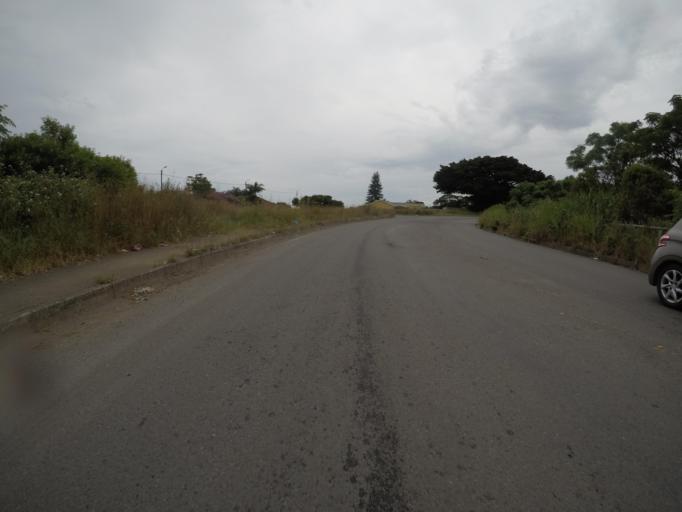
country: ZA
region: Eastern Cape
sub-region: Buffalo City Metropolitan Municipality
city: East London
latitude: -32.9666
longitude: 27.8298
